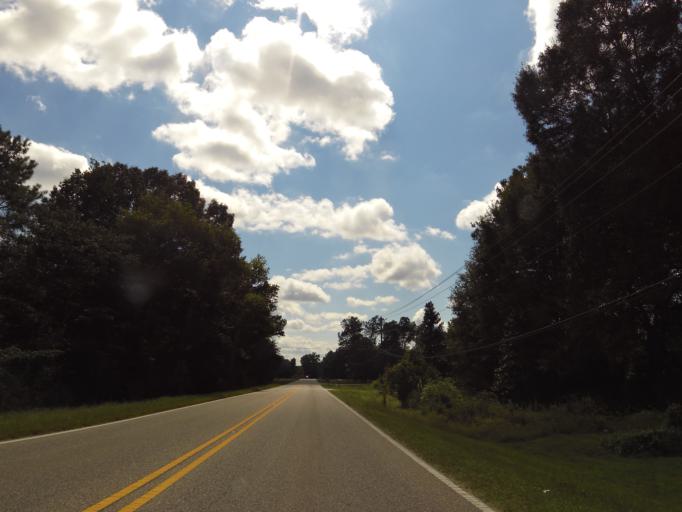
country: US
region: Alabama
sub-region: Dallas County
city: Selma
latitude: 32.4115
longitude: -87.0831
